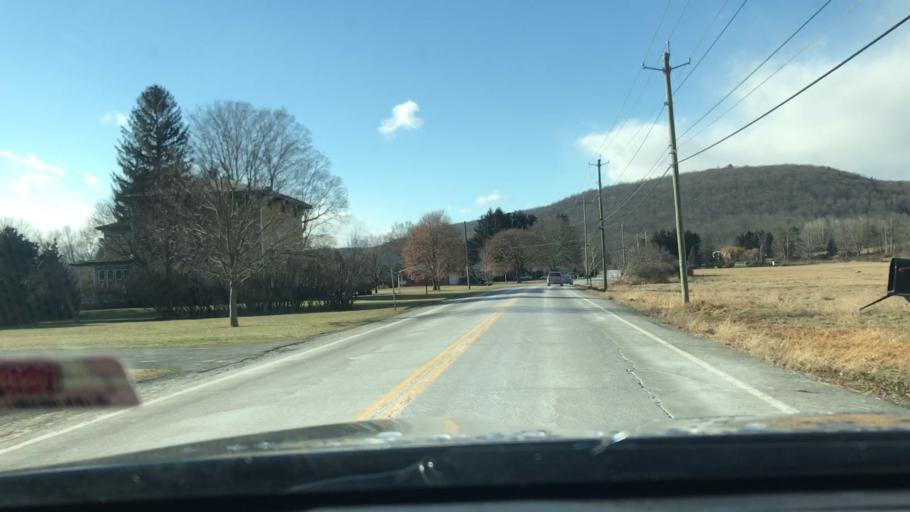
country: US
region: New York
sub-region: Chemung County
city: Big Flats
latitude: 42.1593
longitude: -76.9151
